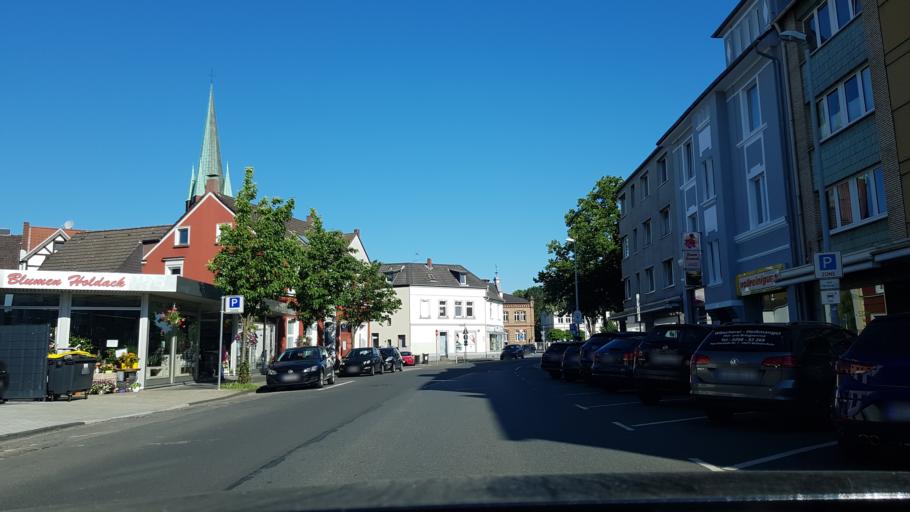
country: DE
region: North Rhine-Westphalia
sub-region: Regierungsbezirk Dusseldorf
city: Muelheim (Ruhr)
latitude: 51.4327
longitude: 6.9257
